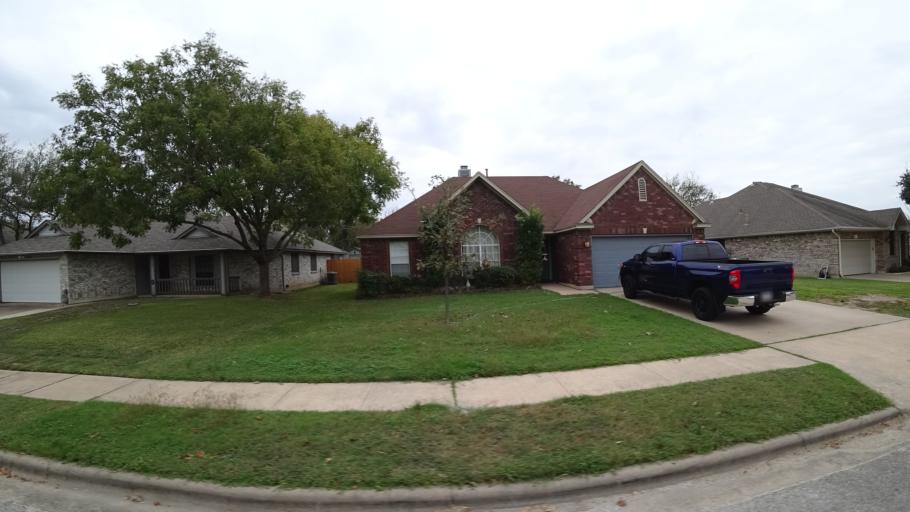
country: US
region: Texas
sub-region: Travis County
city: Pflugerville
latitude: 30.4450
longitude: -97.6241
